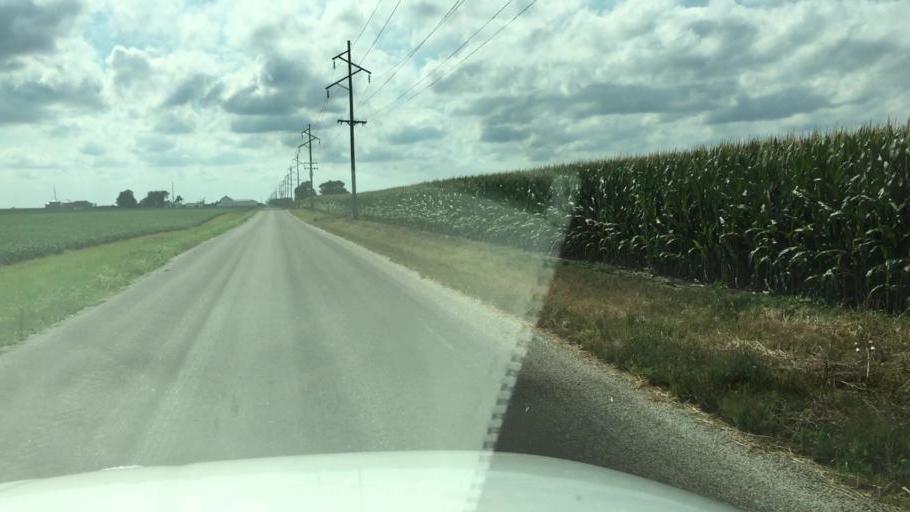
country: US
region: Illinois
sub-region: Hancock County
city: Carthage
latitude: 40.4168
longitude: -91.1691
